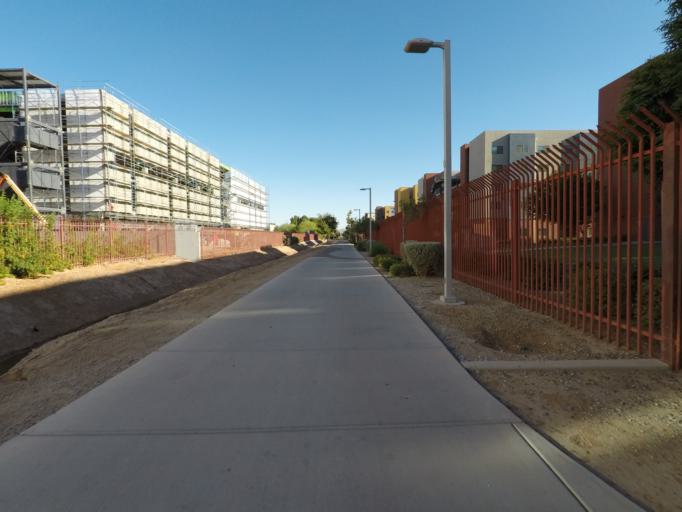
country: US
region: Arizona
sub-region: Maricopa County
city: Glendale
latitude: 33.5147
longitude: -112.1257
